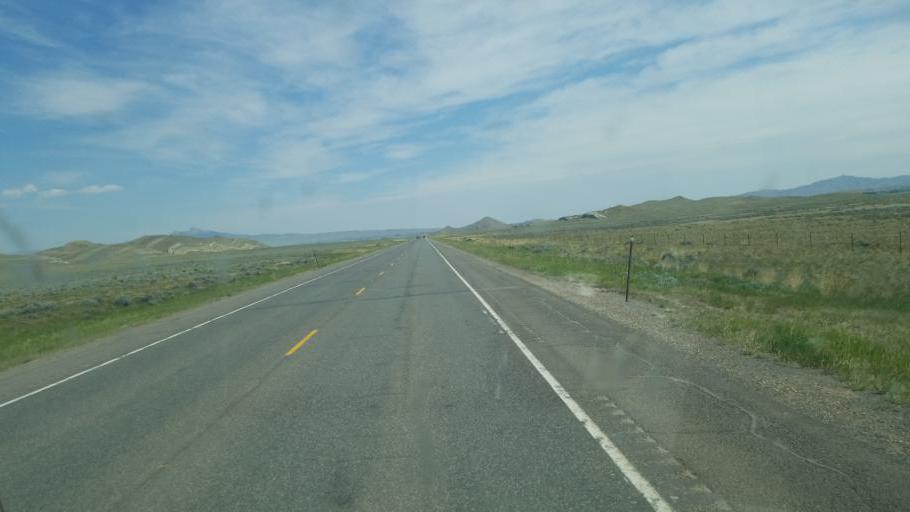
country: US
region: Wyoming
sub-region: Park County
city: Cody
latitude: 44.4520
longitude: -109.0161
